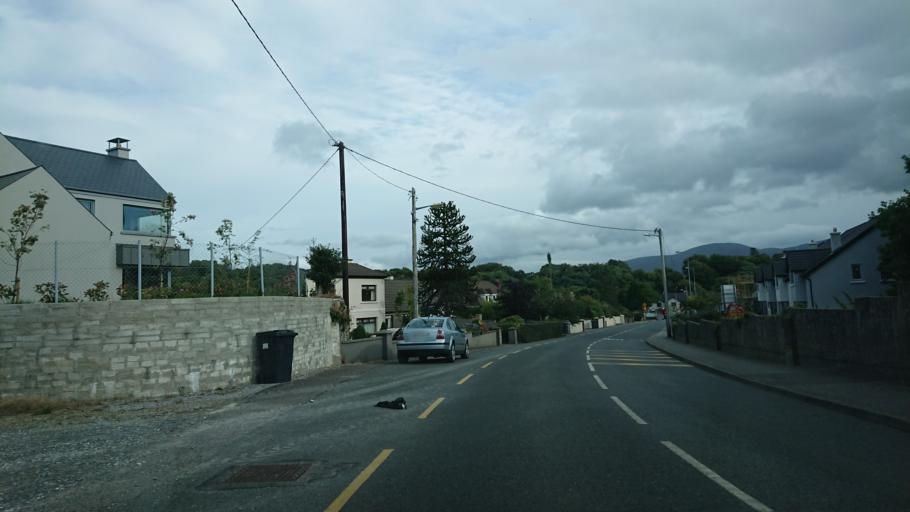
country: IE
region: Munster
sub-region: Ciarrai
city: Cill Airne
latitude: 52.0547
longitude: -9.4898
